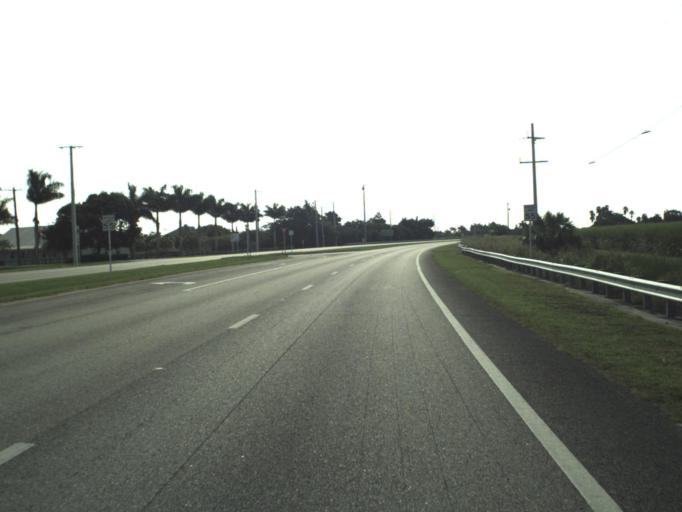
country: US
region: Florida
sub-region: Palm Beach County
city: South Bay
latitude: 26.6801
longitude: -80.7332
